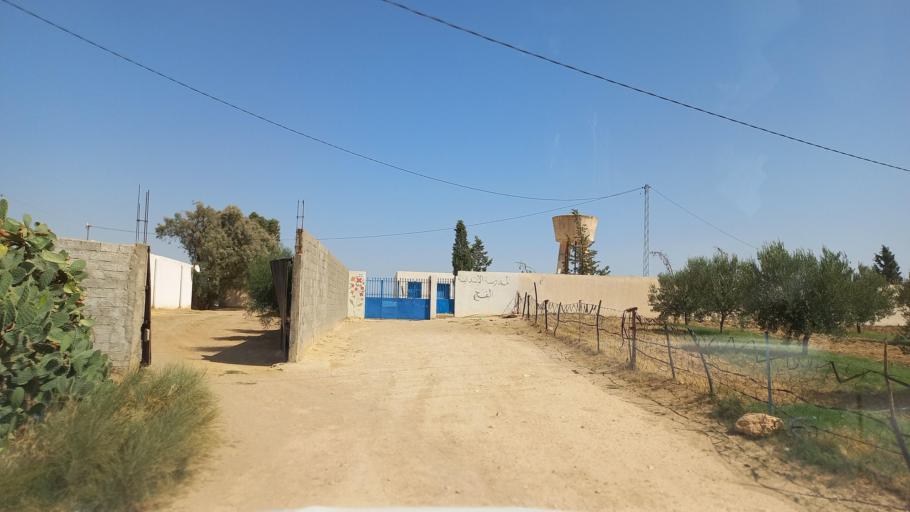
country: TN
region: Al Qasrayn
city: Kasserine
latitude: 35.2099
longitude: 9.0415
